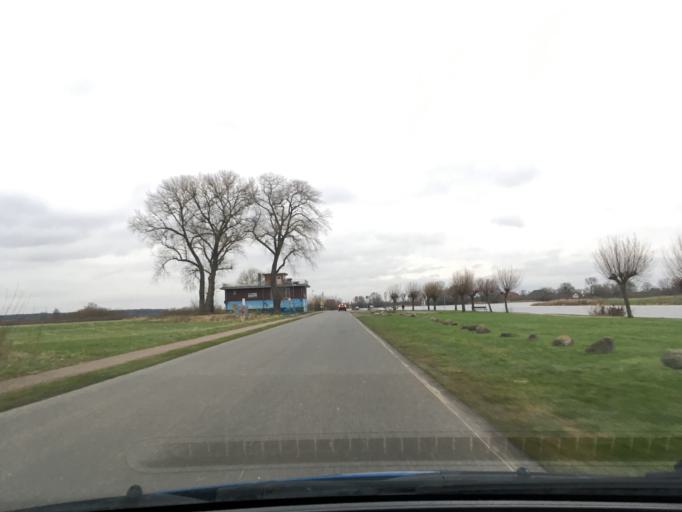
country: DE
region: Lower Saxony
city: Bleckede
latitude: 53.2969
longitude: 10.7343
